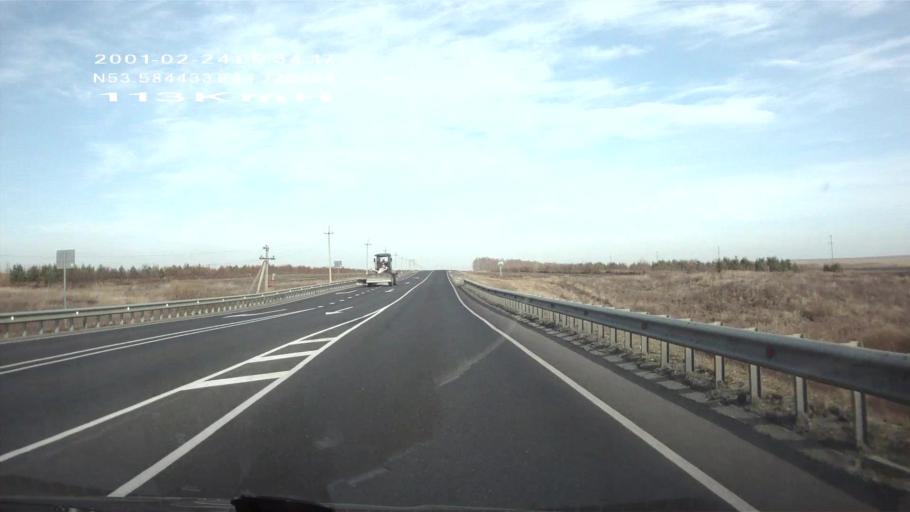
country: RU
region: Penza
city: Mokshan
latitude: 53.5849
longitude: 44.7278
